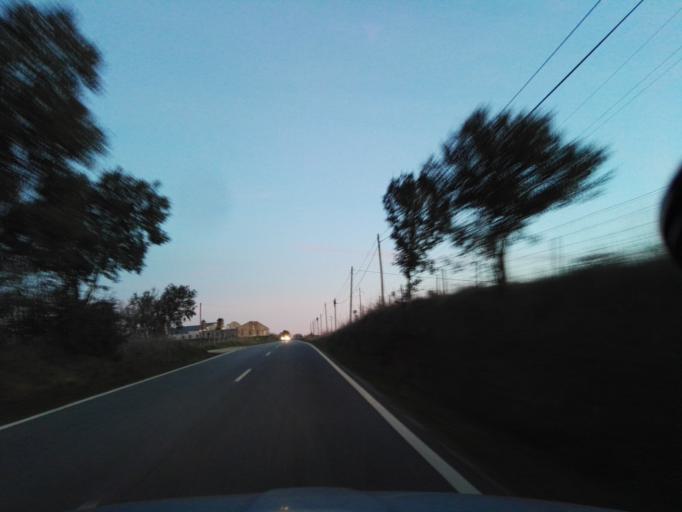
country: PT
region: Evora
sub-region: Arraiolos
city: Arraiolos
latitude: 38.7195
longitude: -8.0520
